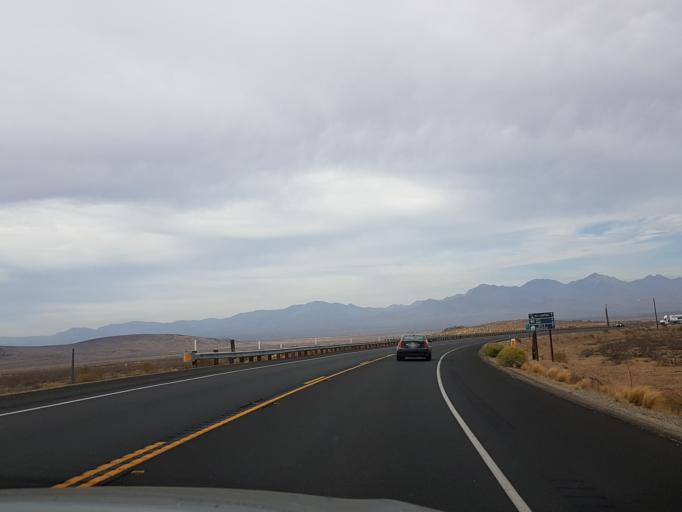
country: US
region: California
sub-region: Kern County
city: Ridgecrest
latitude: 35.5489
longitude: -117.7110
